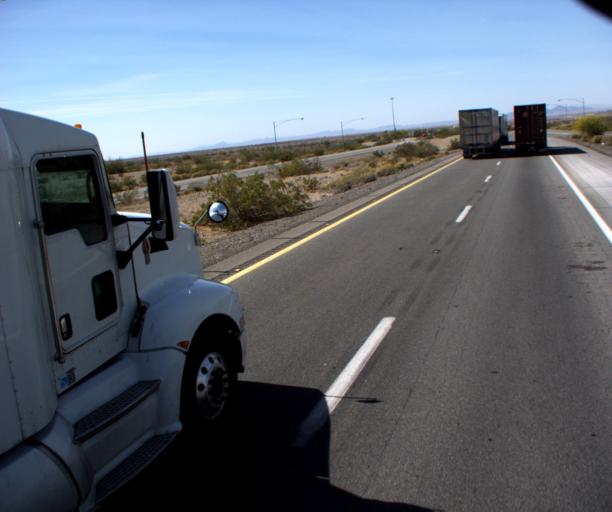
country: US
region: Arizona
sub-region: La Paz County
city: Ehrenberg
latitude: 33.6204
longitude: -114.4481
